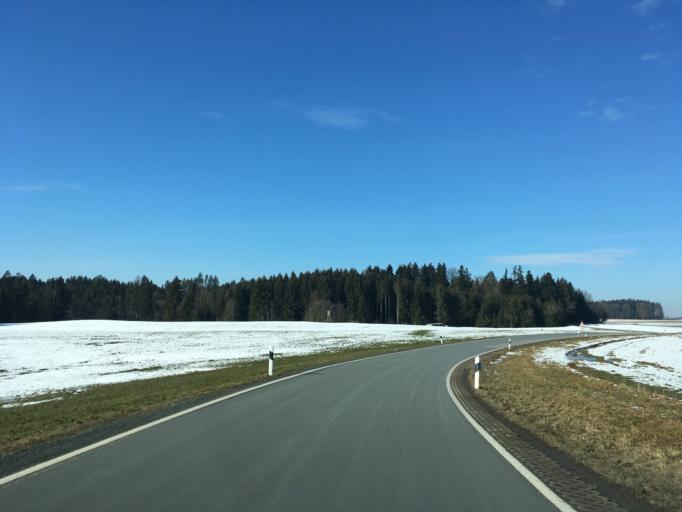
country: DE
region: Bavaria
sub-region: Upper Bavaria
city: Ramerberg
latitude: 48.0068
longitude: 12.1434
